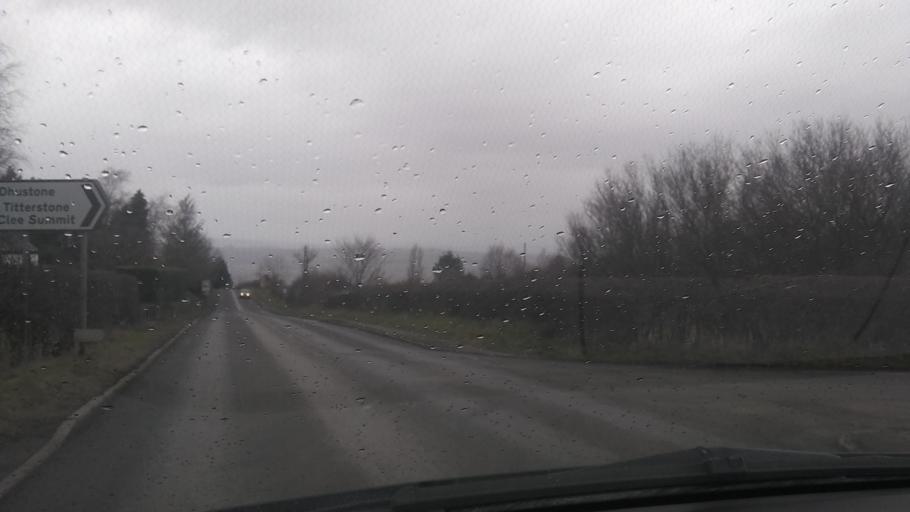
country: GB
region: England
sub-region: Worcestershire
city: Tenbury Wells
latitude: 52.3787
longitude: -2.6190
